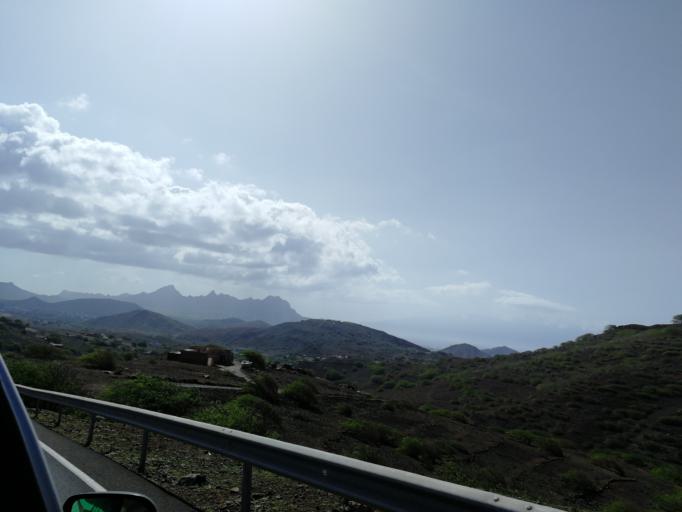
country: CV
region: Sao Vicente
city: Mindelo
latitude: 16.8756
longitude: -24.9489
